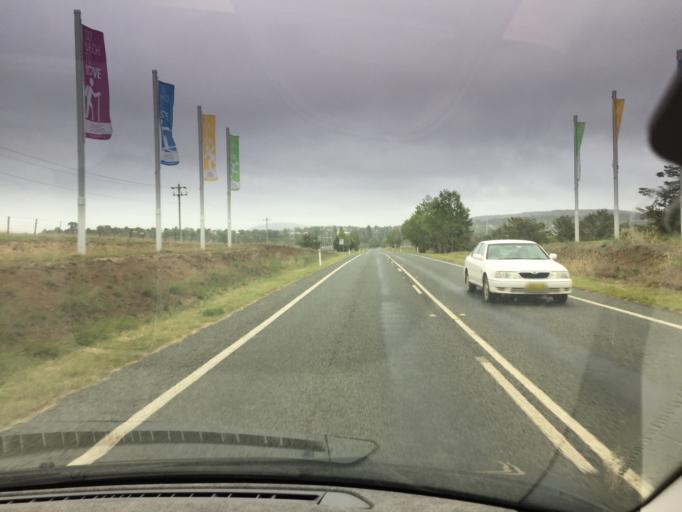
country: AU
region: New South Wales
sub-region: Cooma-Monaro
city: Cooma
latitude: -36.2147
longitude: 149.1474
